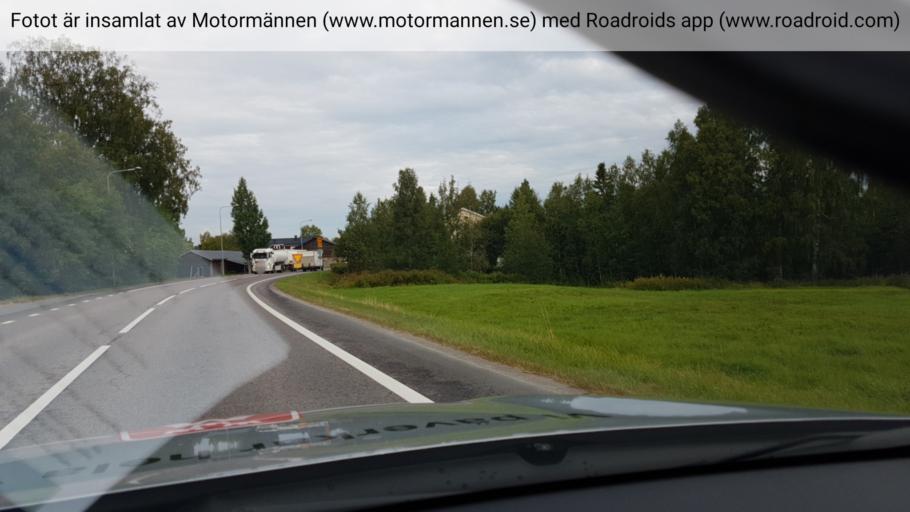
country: SE
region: Norrbotten
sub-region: Lulea Kommun
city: Gammelstad
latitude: 65.5849
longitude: 22.0313
